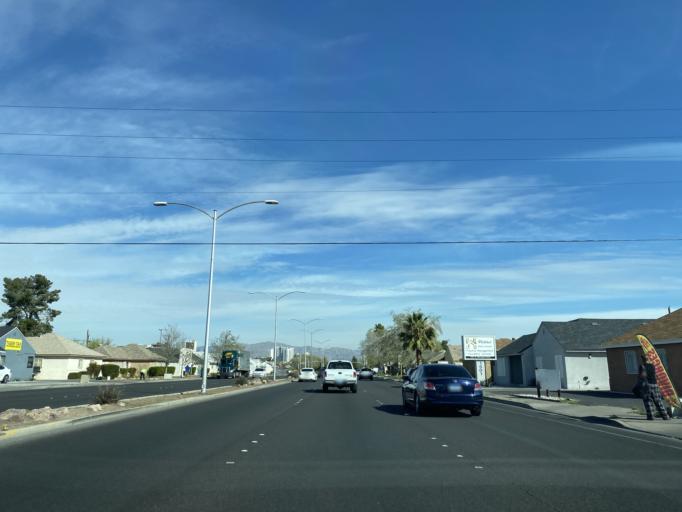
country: US
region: Nevada
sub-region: Clark County
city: Las Vegas
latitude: 36.1524
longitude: -115.1369
